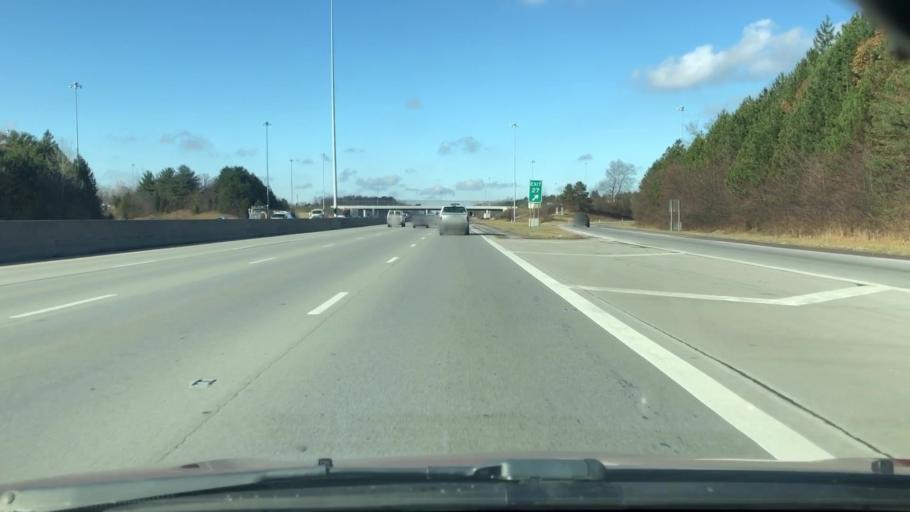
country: US
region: Ohio
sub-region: Franklin County
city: Westerville
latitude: 40.1052
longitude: -82.9435
